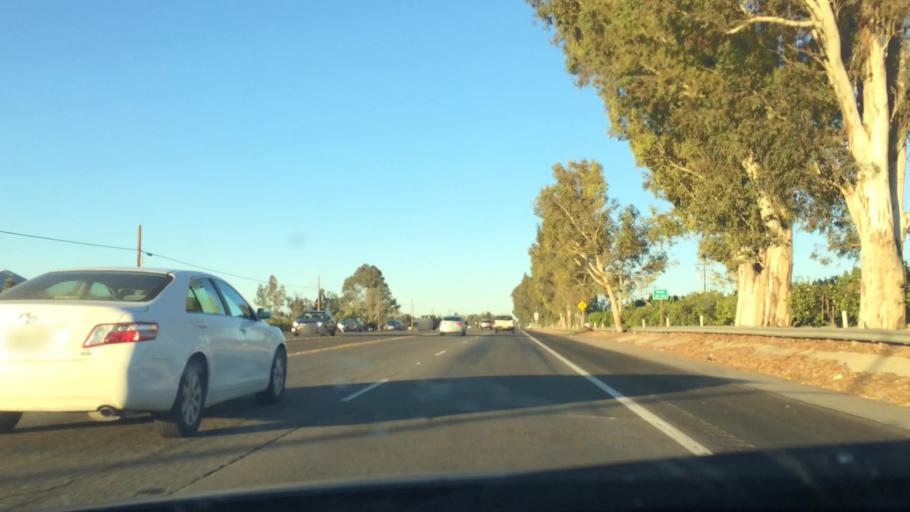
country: US
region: California
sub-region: Ventura County
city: Fillmore
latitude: 34.3827
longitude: -118.9695
